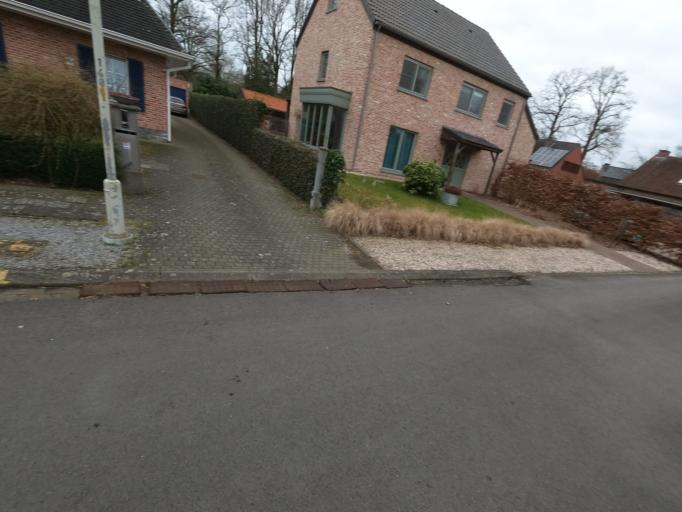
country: BE
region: Flanders
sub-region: Provincie Antwerpen
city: Kalmthout
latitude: 51.3963
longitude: 4.4600
